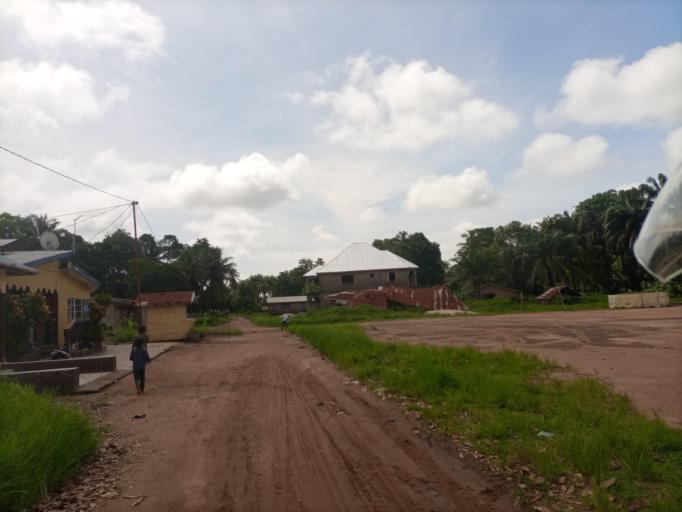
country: SL
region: Northern Province
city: Masoyila
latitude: 8.6195
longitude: -13.1734
